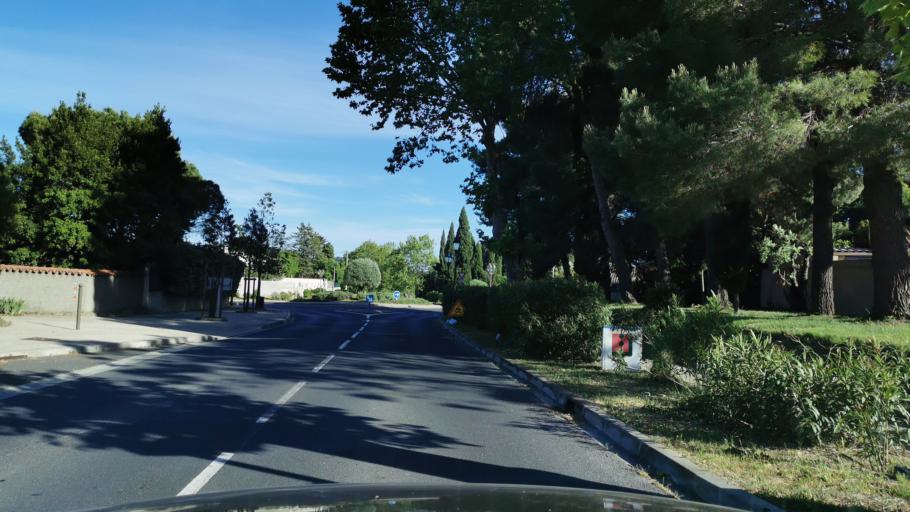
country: FR
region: Languedoc-Roussillon
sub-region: Departement de l'Aude
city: Marcorignan
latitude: 43.2232
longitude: 2.9236
